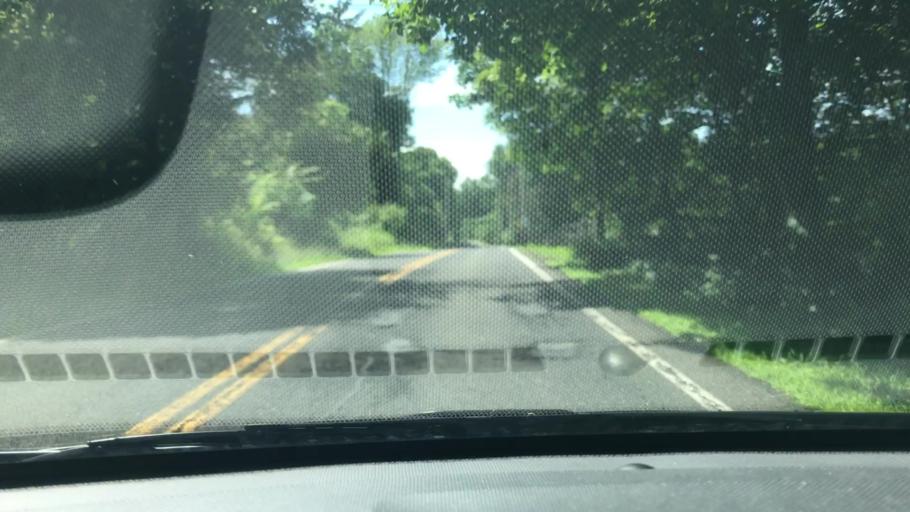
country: US
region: New York
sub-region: Ulster County
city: Stone Ridge
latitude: 41.8893
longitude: -74.1598
